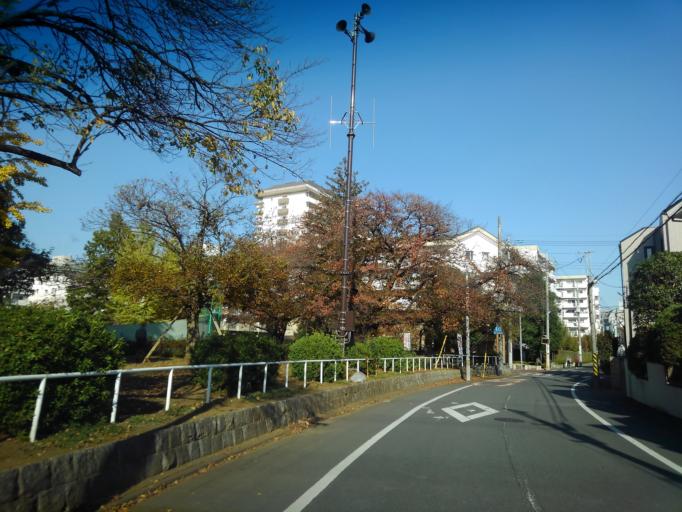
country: JP
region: Saitama
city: Tokorozawa
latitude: 35.8033
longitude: 139.4534
